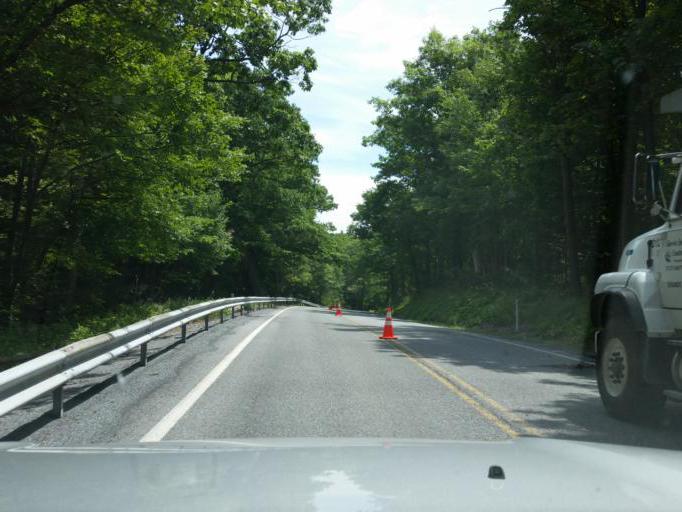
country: US
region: Pennsylvania
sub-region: Blair County
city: Altoona
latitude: 40.5649
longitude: -78.4505
